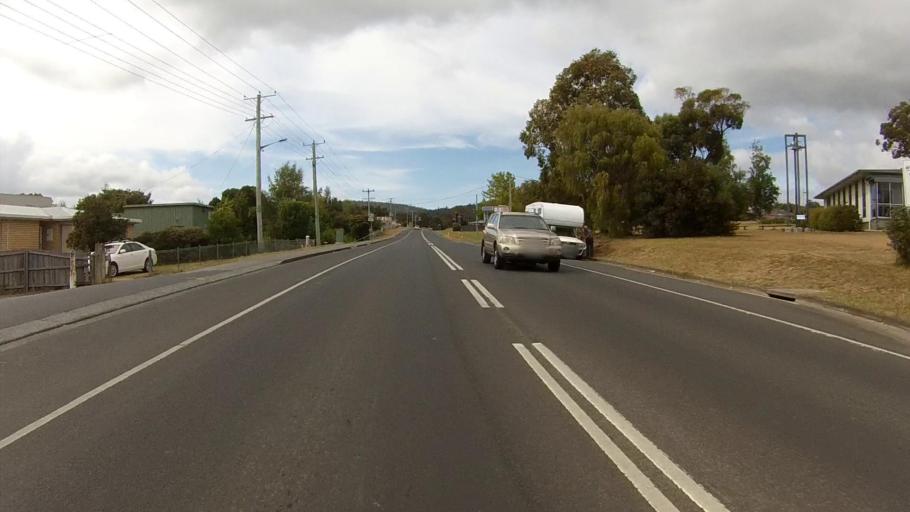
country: AU
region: Tasmania
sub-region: Kingborough
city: Margate
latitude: -43.0665
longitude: 147.2553
